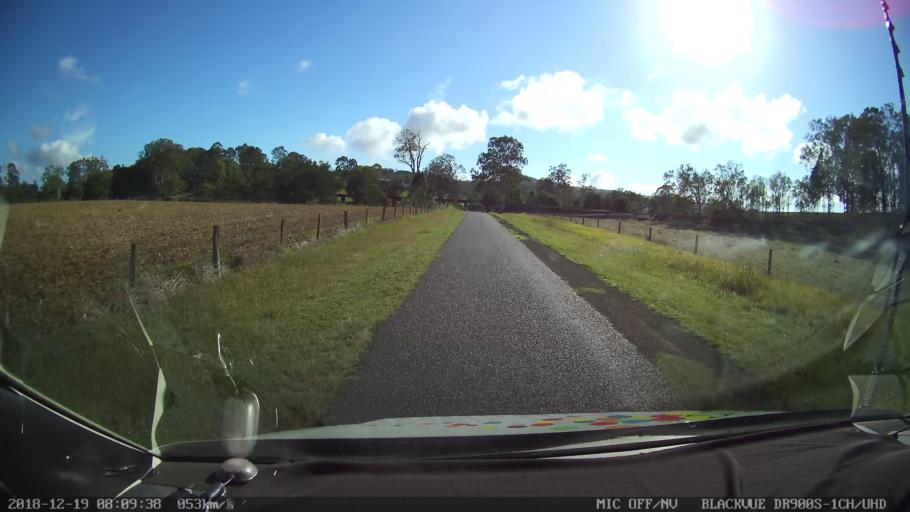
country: AU
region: Queensland
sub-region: Logan
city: Cedar Vale
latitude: -28.2136
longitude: 152.8804
